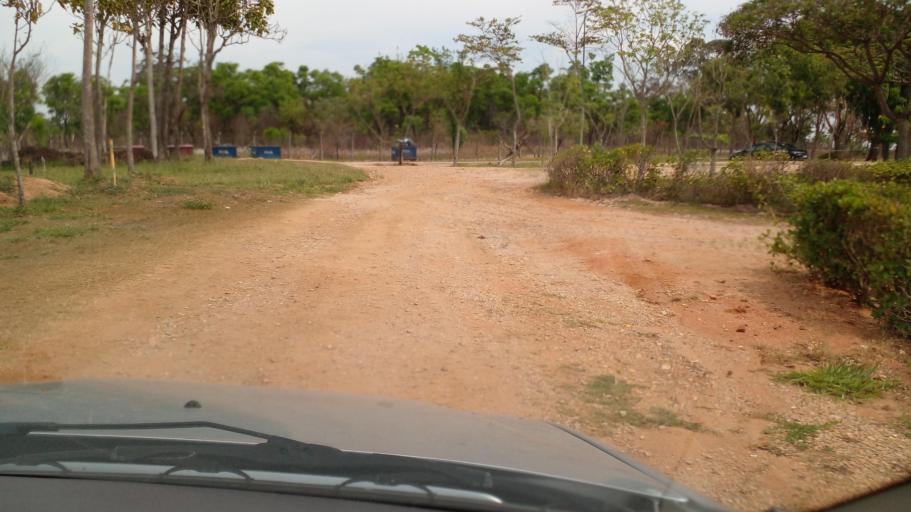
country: BR
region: Sao Paulo
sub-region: Jundiai
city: Jundiai
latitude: -23.1507
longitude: -46.8808
